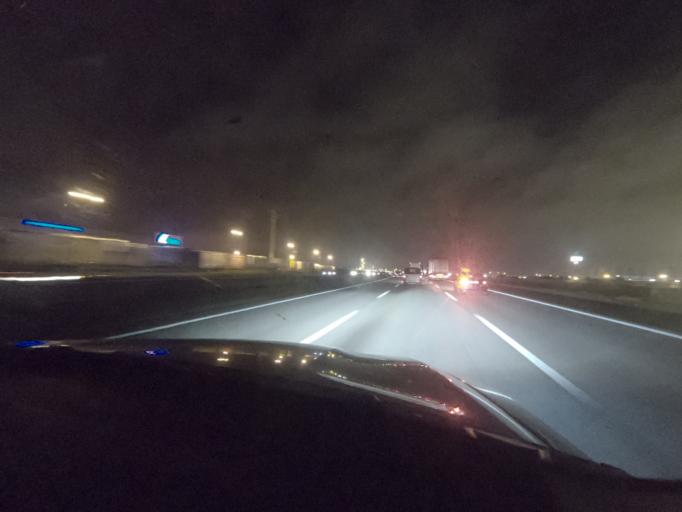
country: PT
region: Lisbon
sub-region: Alenquer
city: Carregado
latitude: 39.0330
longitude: -8.9601
